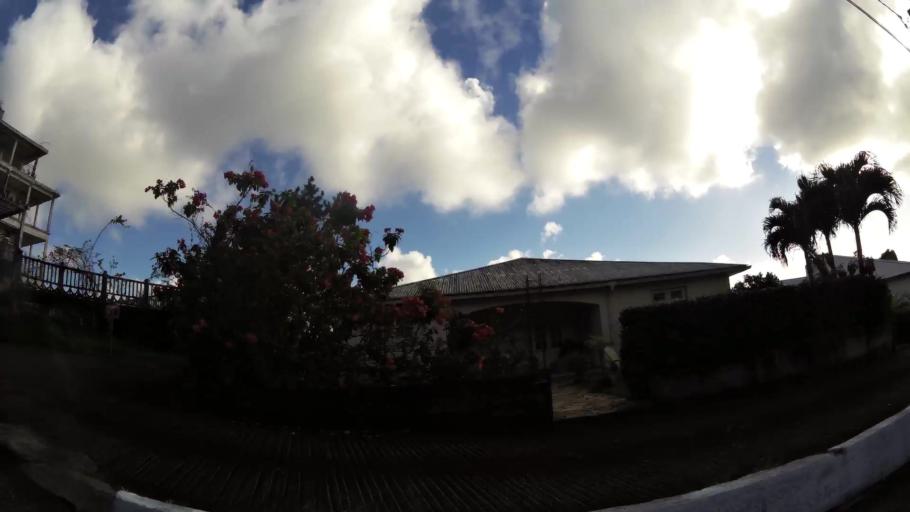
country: MQ
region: Martinique
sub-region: Martinique
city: Saint-Joseph
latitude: 14.6562
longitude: -61.0853
